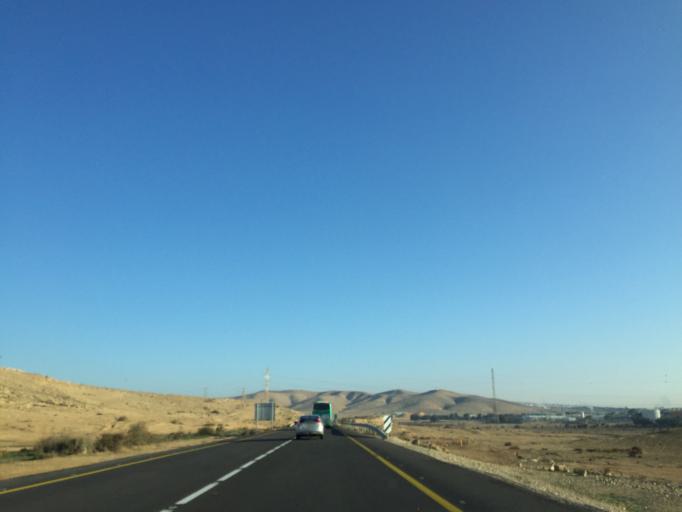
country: IL
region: Southern District
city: Dimona
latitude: 31.0579
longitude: 35.0001
